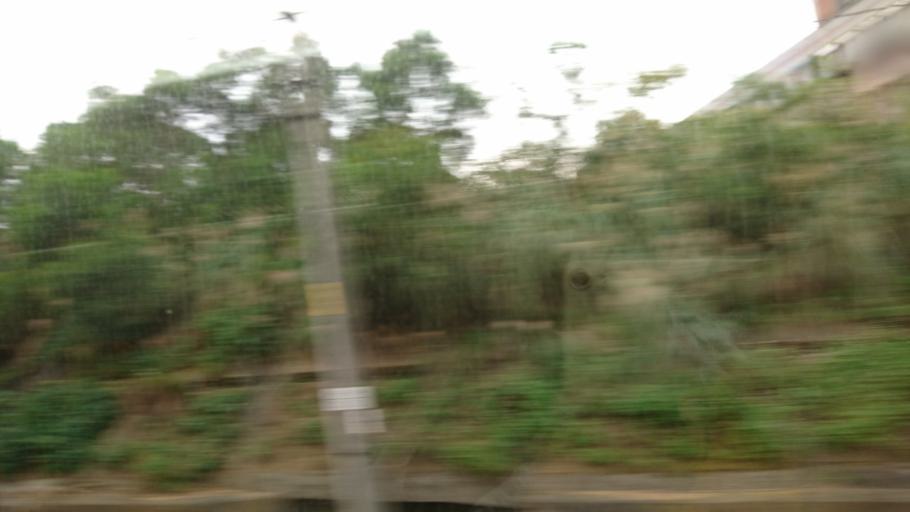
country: TW
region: Taiwan
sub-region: Hsinchu
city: Zhubei
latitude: 24.8623
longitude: 120.9937
